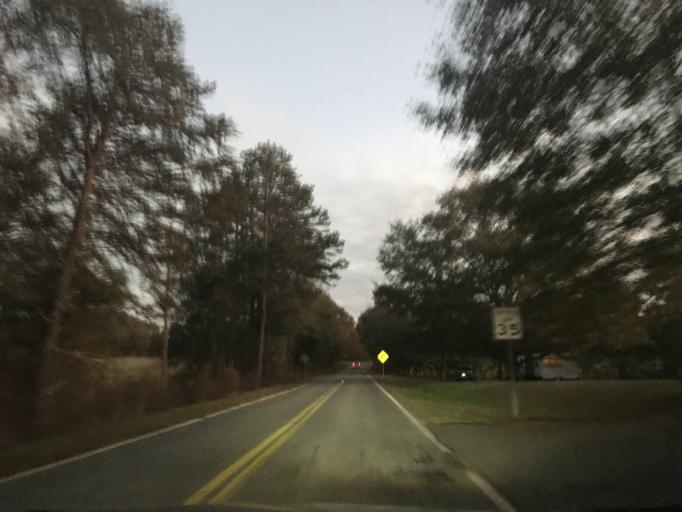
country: US
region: South Carolina
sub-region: Spartanburg County
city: Mayo
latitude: 35.0727
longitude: -81.9012
